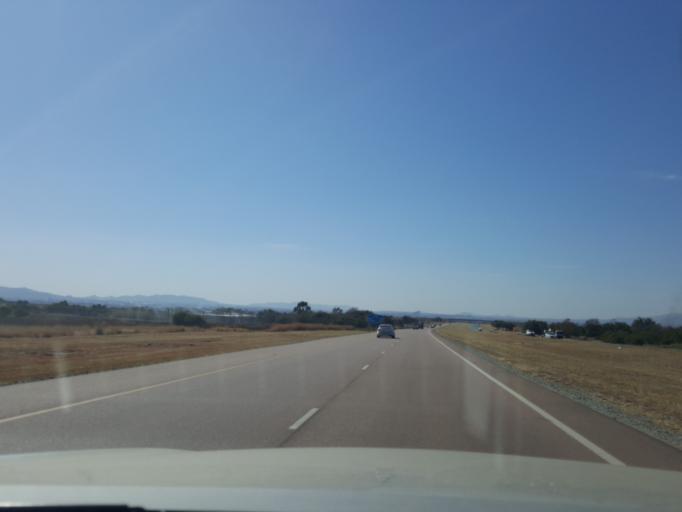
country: ZA
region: North-West
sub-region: Bojanala Platinum District Municipality
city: Brits
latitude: -25.6905
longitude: 27.7451
